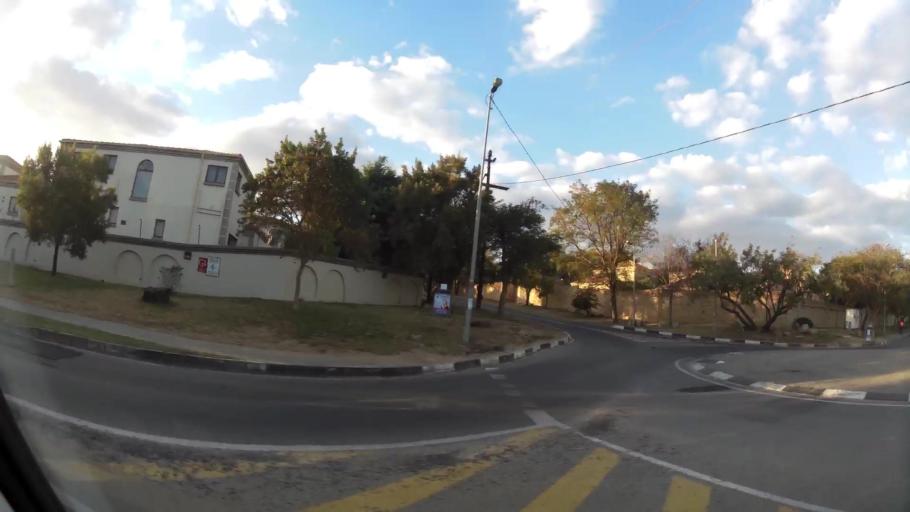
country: ZA
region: Gauteng
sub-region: City of Johannesburg Metropolitan Municipality
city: Diepsloot
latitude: -26.0178
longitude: 27.9921
